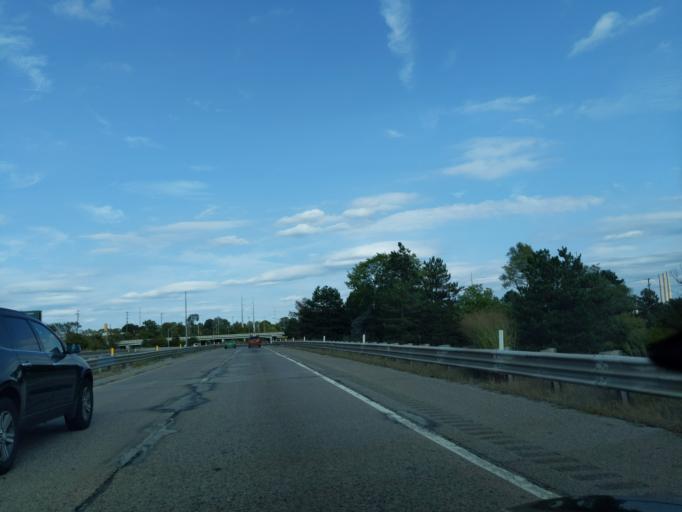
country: US
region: Michigan
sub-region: Ingham County
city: Edgemont Park
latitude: 42.7248
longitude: -84.5882
